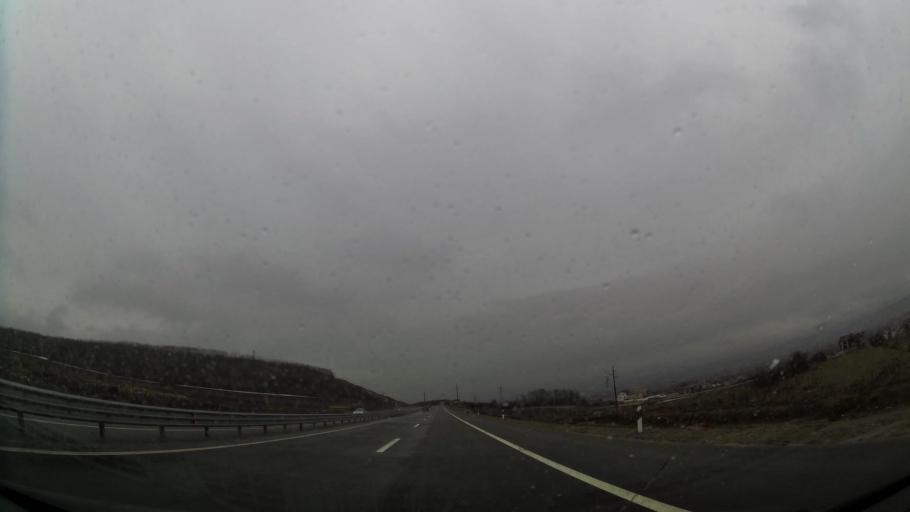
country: XK
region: Ferizaj
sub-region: Komuna e Ferizajt
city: Ferizaj
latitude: 42.3280
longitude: 21.2048
